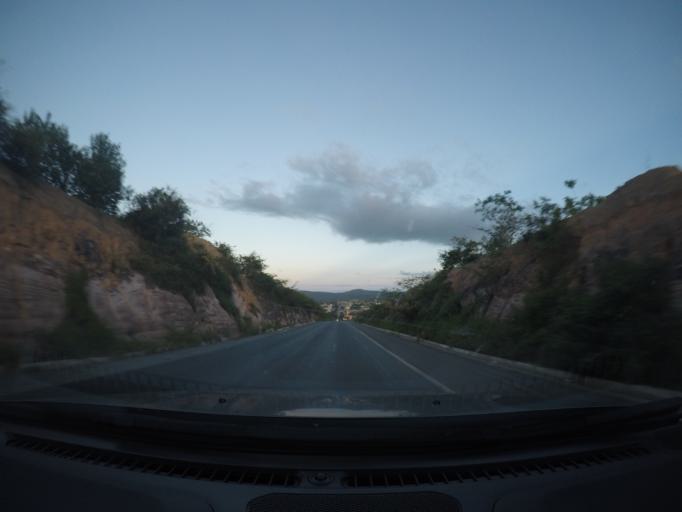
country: BR
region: Bahia
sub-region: Seabra
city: Seabra
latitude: -12.4292
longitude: -41.7854
